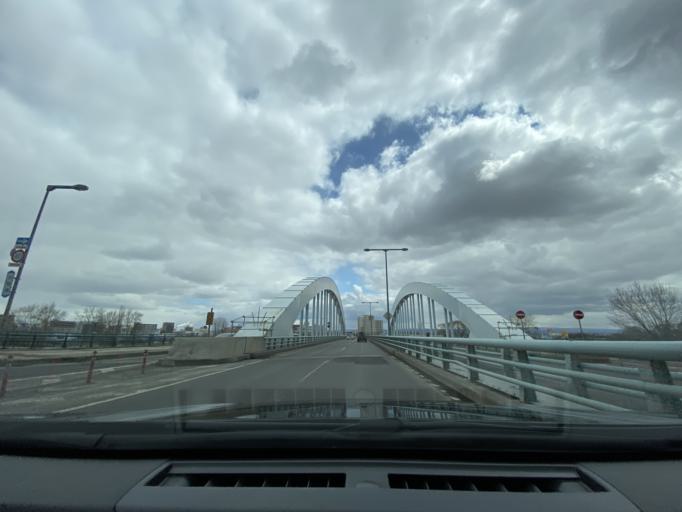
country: JP
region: Hokkaido
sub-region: Asahikawa-shi
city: Asahikawa
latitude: 43.7546
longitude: 142.3654
